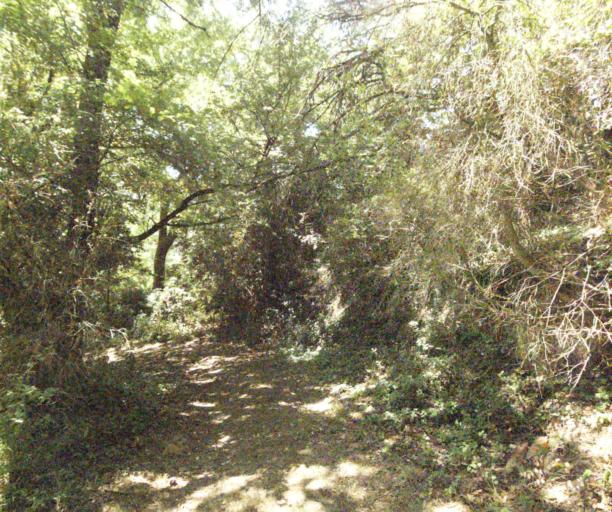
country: FR
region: Midi-Pyrenees
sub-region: Departement de la Haute-Garonne
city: Saint-Felix-Lauragais
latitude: 43.4781
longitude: 1.8595
